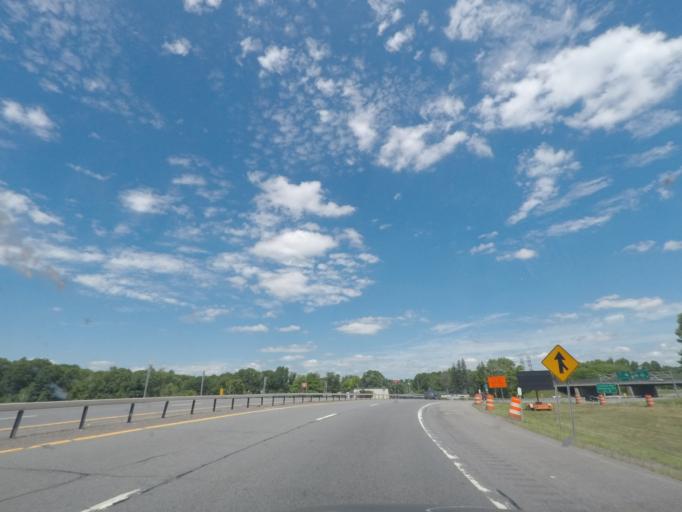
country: US
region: New York
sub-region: Schenectady County
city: Rotterdam
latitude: 42.7583
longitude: -73.9332
